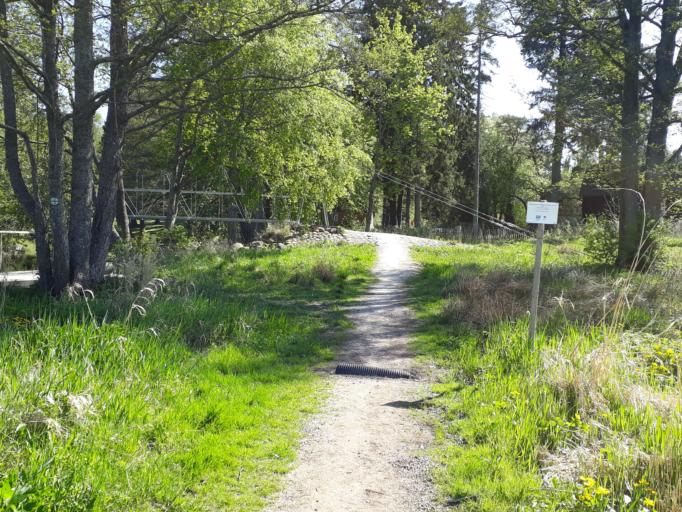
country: EE
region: Laeaene-Virumaa
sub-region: Haljala vald
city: Haljala
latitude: 59.5861
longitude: 26.1178
